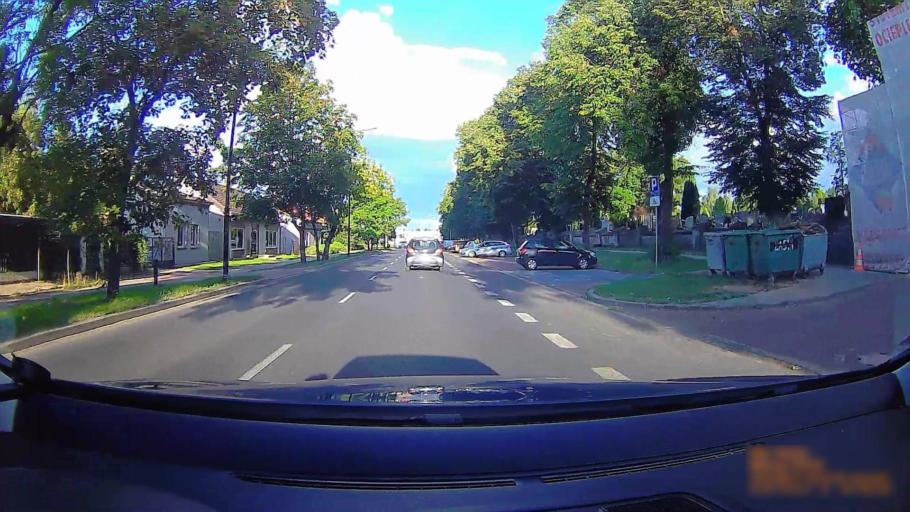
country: PL
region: Greater Poland Voivodeship
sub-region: Konin
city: Konin
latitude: 52.2035
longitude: 18.2675
